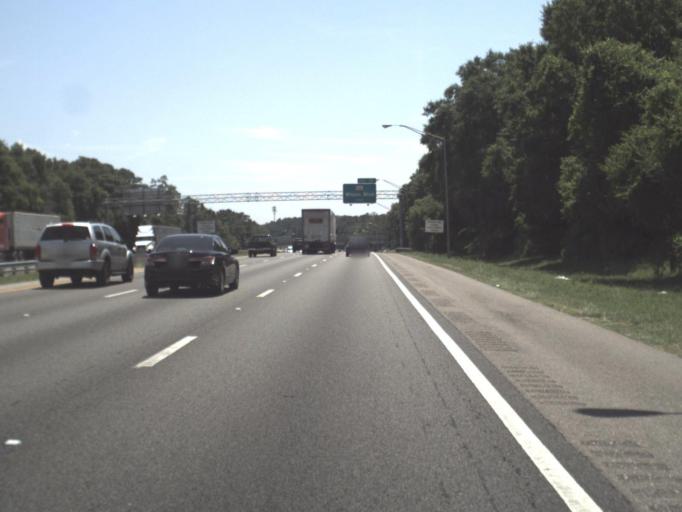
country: US
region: Florida
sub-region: Clay County
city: Bellair-Meadowbrook Terrace
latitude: 30.2893
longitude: -81.7716
